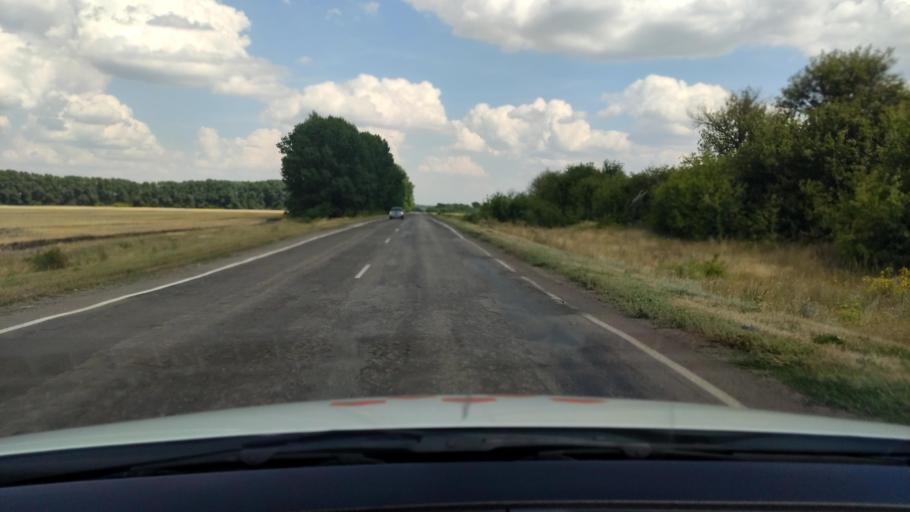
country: RU
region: Voronezj
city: Ertil'
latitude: 51.7901
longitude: 40.6668
